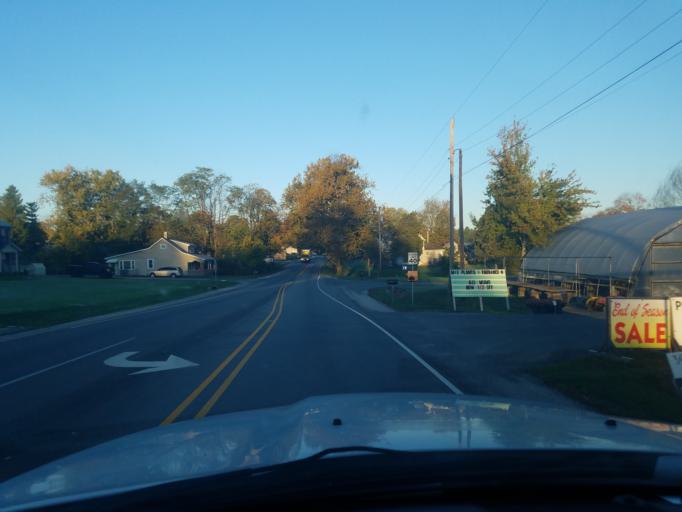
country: US
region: Indiana
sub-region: Floyd County
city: Galena
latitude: 38.3511
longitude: -85.9387
